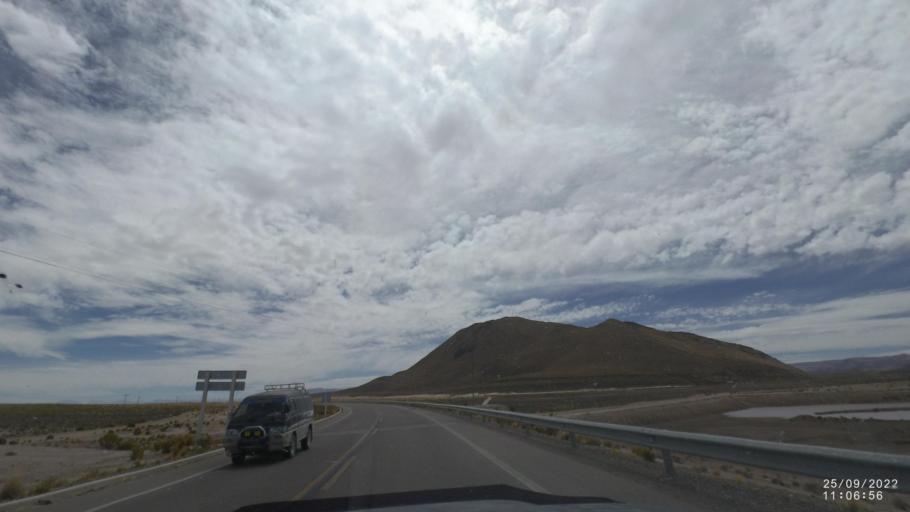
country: BO
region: Oruro
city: Challapata
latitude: -19.3523
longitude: -66.8563
